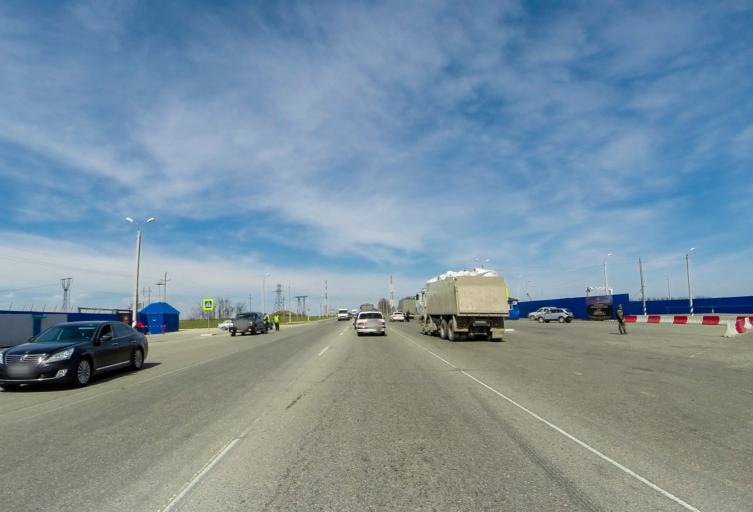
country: RU
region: Kabardino-Balkariya
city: Malka
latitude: 43.8058
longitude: 43.3668
